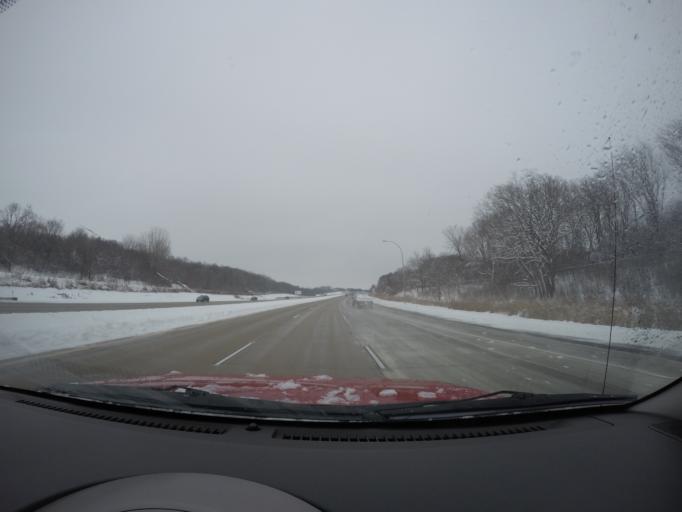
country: US
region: Minnesota
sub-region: Olmsted County
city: Rochester
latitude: 43.9784
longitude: -92.4681
